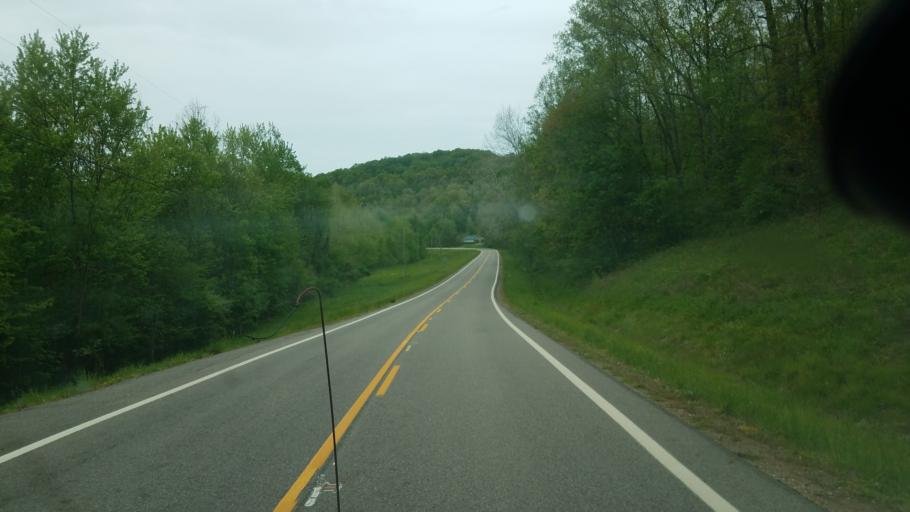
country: US
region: Ohio
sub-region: Guernsey County
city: Mantua
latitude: 40.1613
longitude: -81.6415
